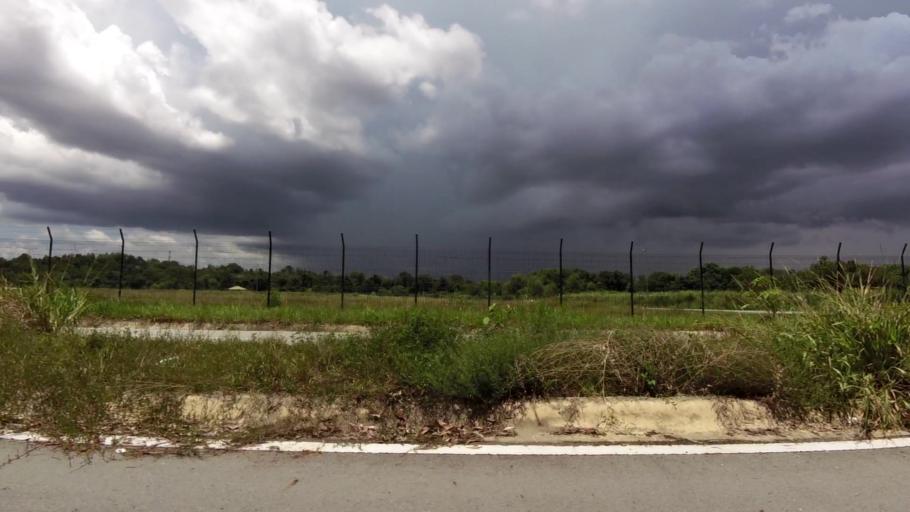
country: BN
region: Brunei and Muara
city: Bandar Seri Begawan
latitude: 4.9413
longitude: 114.8849
